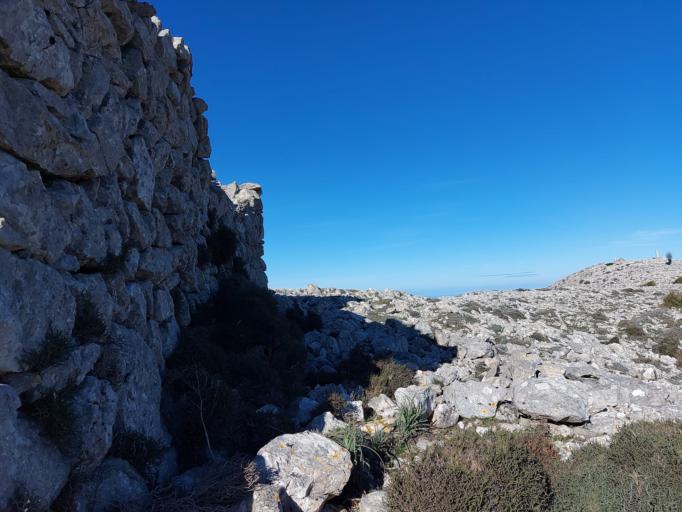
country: ES
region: Balearic Islands
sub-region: Illes Balears
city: Estellencs
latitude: 39.6246
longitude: 2.4462
